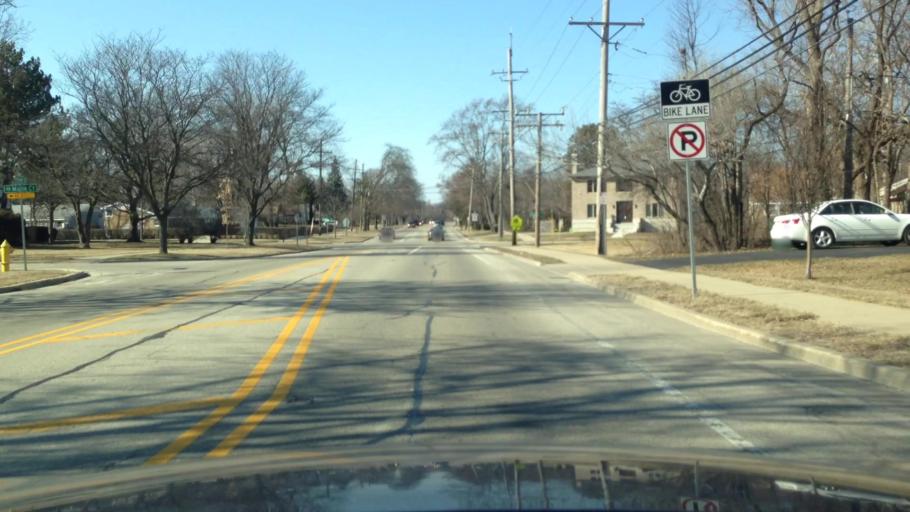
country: US
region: Illinois
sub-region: Cook County
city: Glenview
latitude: 42.0615
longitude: -87.8149
